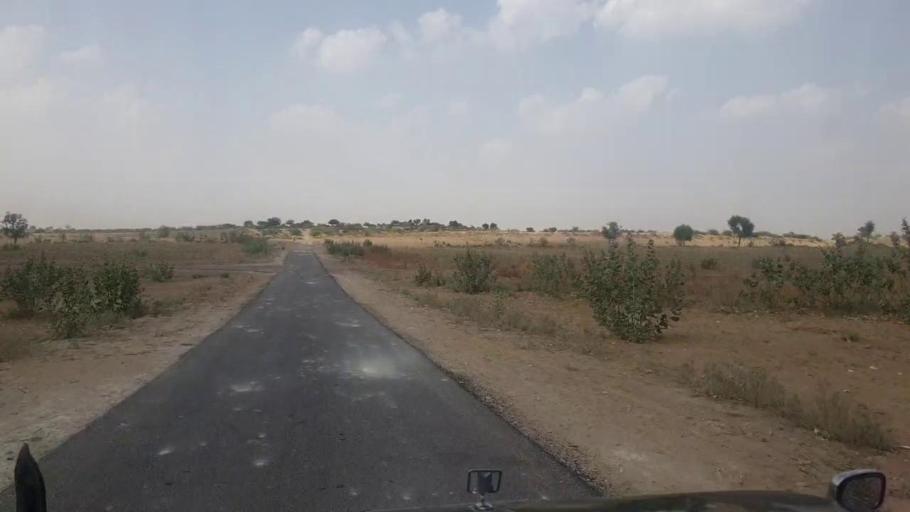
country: PK
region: Sindh
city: Islamkot
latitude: 25.2292
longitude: 70.2860
